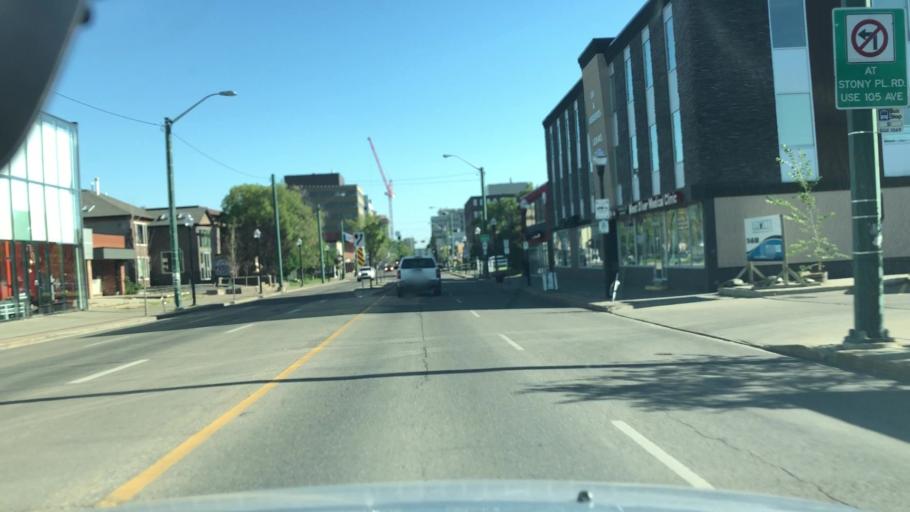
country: CA
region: Alberta
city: Edmonton
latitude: 53.5491
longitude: -113.5359
